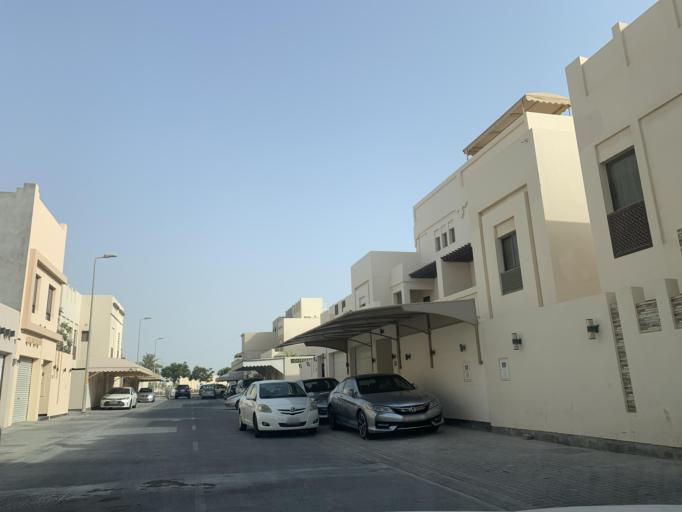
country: BH
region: Manama
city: Jidd Hafs
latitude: 26.2274
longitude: 50.4438
